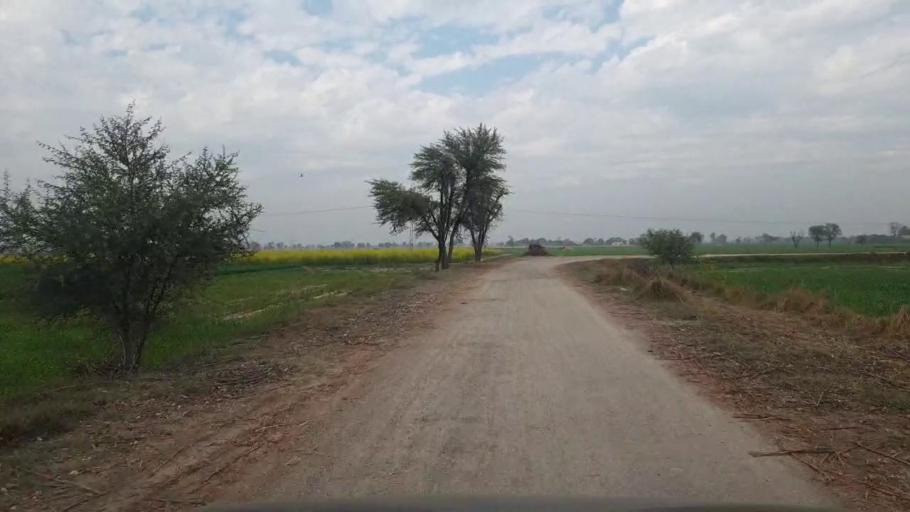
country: PK
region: Sindh
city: Sakrand
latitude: 26.0305
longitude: 68.4070
